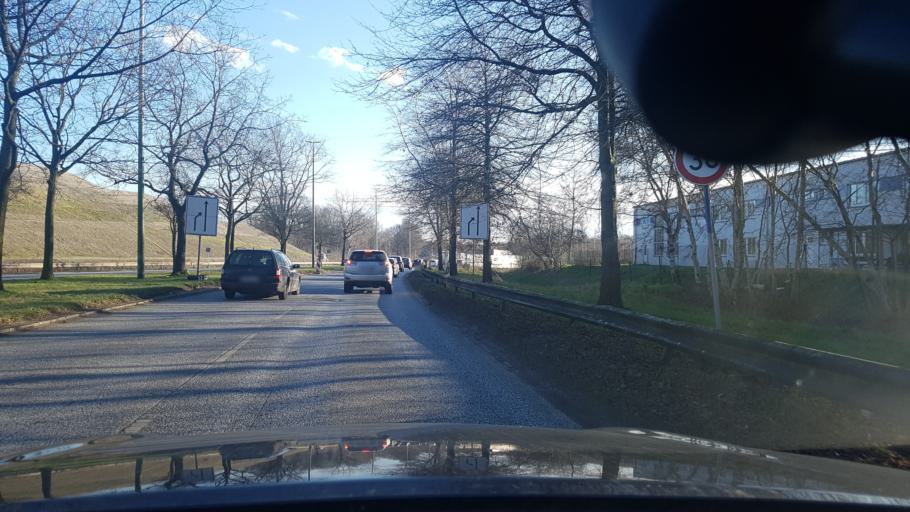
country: DE
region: Lower Saxony
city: Langen
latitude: 53.5859
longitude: 8.6070
